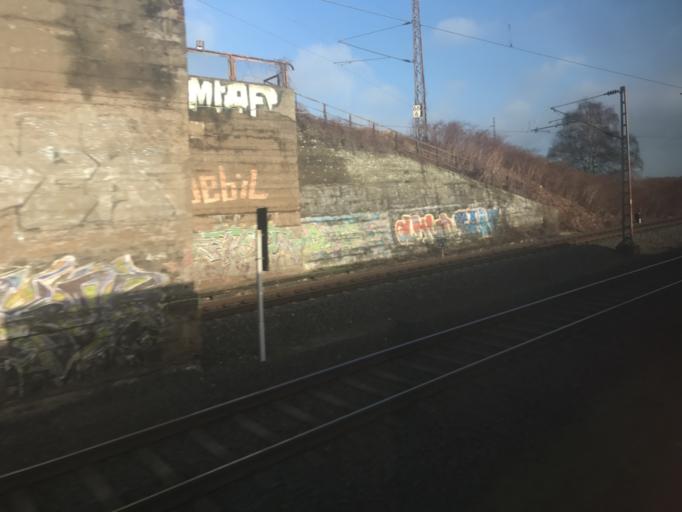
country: DE
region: North Rhine-Westphalia
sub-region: Regierungsbezirk Dusseldorf
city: Duisburg
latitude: 51.4470
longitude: 6.8118
